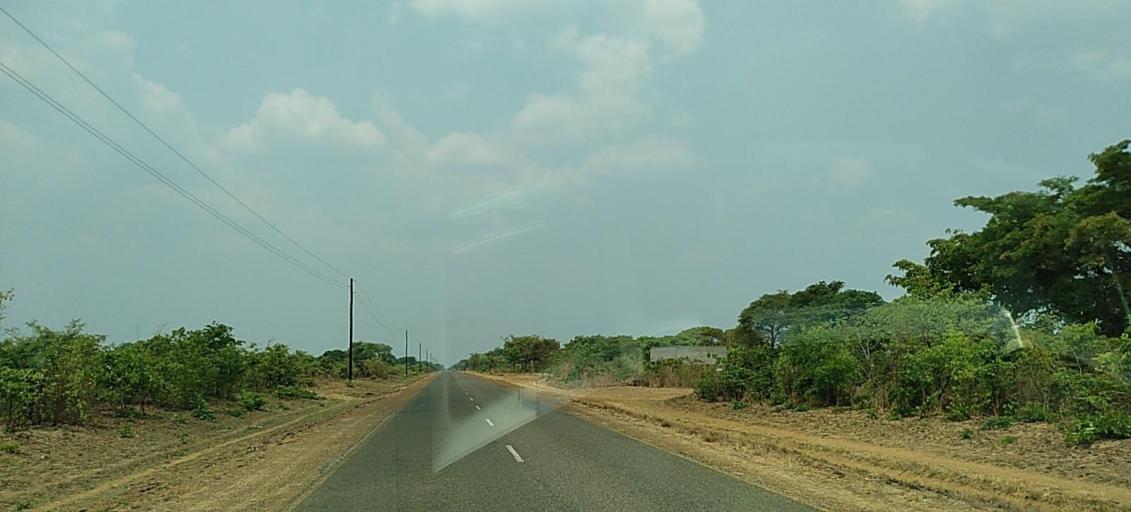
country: ZM
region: North-Western
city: Zambezi
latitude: -13.5519
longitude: 23.1343
